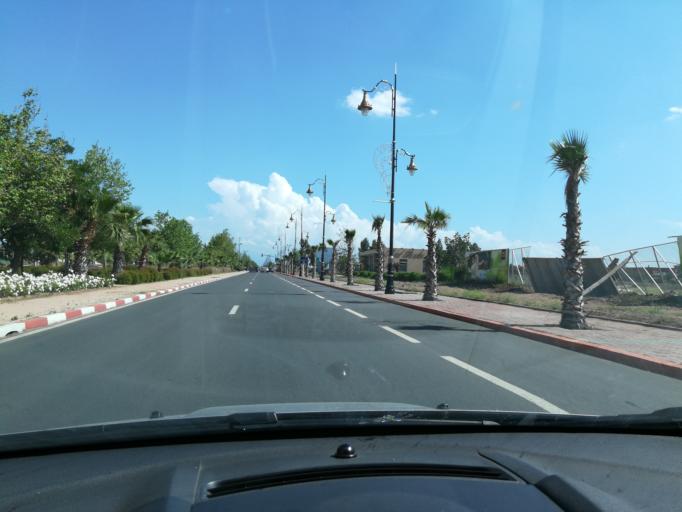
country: MA
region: Marrakech-Tensift-Al Haouz
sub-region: Marrakech
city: Marrakesh
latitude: 31.5970
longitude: -7.9946
